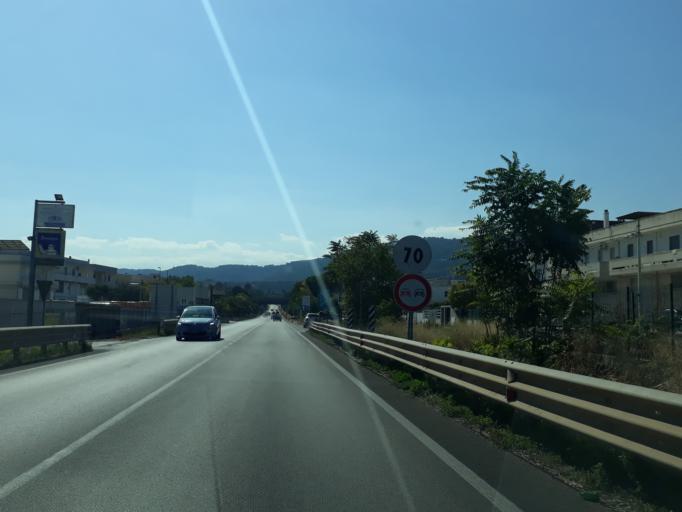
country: IT
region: Apulia
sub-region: Provincia di Brindisi
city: Fasano
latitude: 40.8444
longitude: 17.3543
